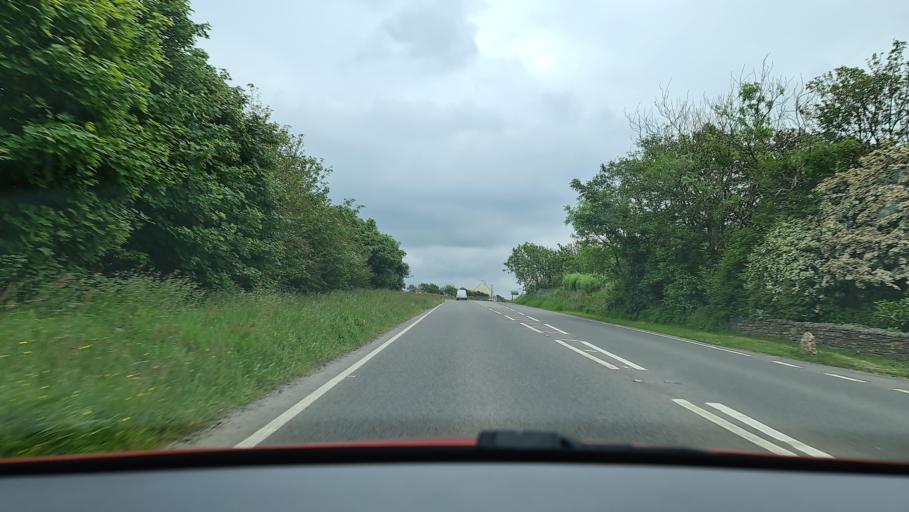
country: GB
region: England
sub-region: Cornwall
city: Camelford
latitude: 50.6526
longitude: -4.6356
